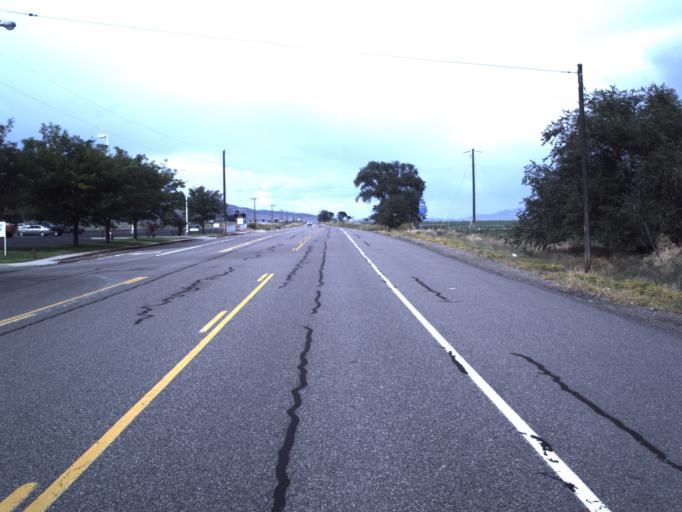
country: US
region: Utah
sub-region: Piute County
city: Junction
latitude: 38.2438
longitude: -112.2200
